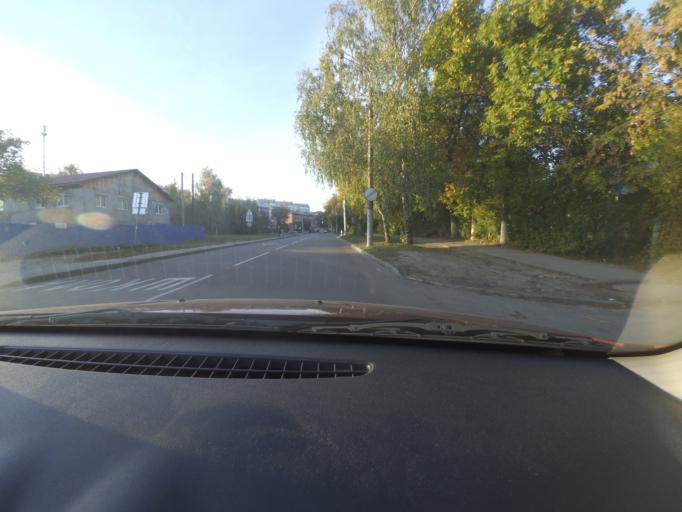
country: RU
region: Nizjnij Novgorod
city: Nizhniy Novgorod
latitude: 56.2745
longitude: 43.9904
